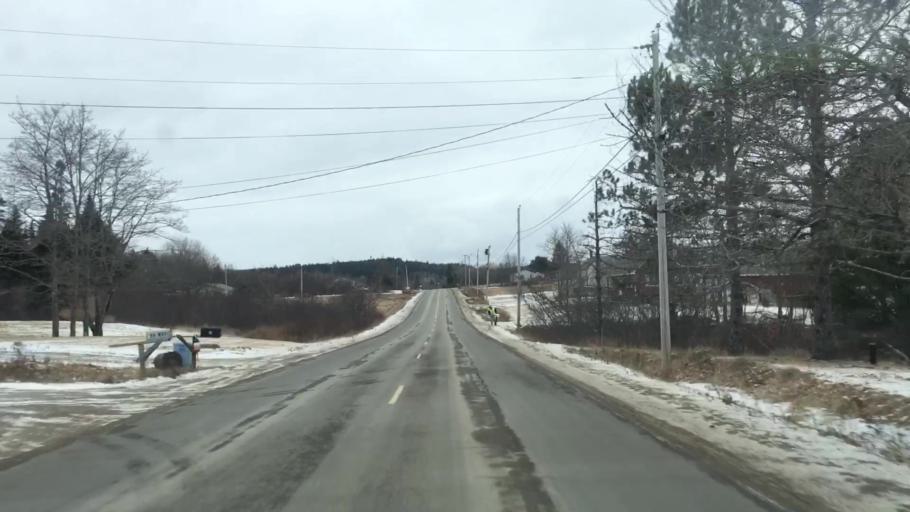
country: US
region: Maine
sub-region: Washington County
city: Machiasport
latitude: 44.7096
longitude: -67.4028
